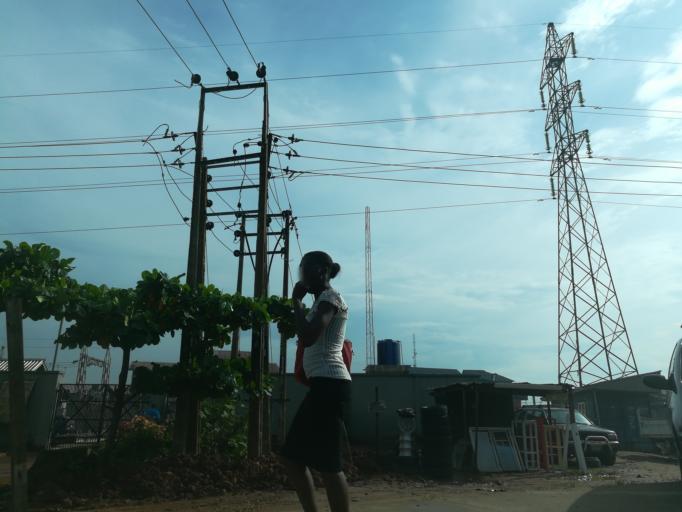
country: NG
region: Lagos
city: Ojota
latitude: 6.6097
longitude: 3.4221
